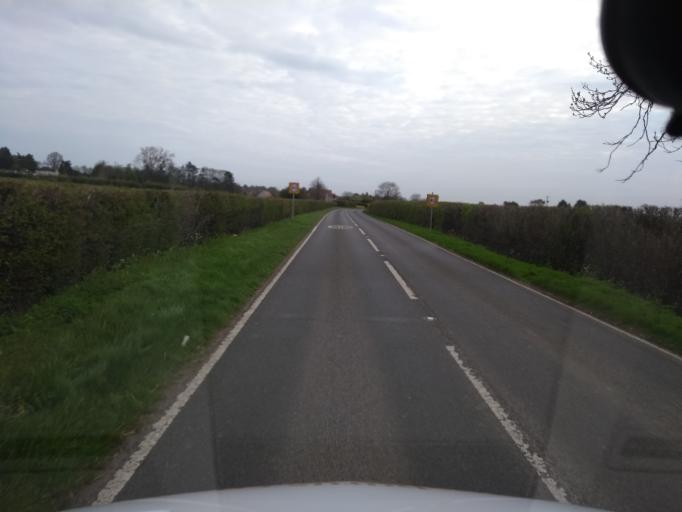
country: GB
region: England
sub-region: Somerset
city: Curry Rivel
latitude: 51.0174
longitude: -2.8872
